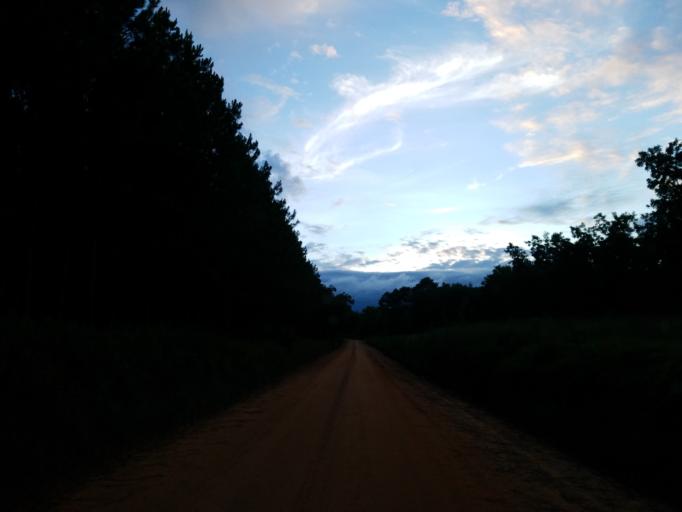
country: US
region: Georgia
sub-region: Tift County
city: Tifton
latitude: 31.5315
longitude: -83.5121
